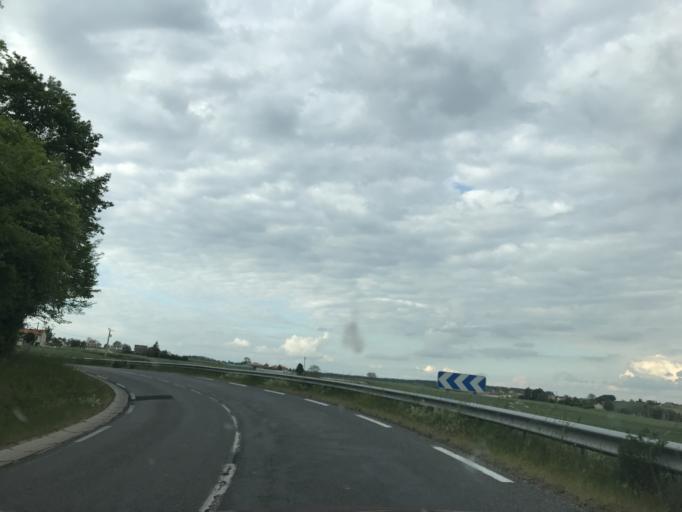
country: FR
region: Auvergne
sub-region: Departement du Puy-de-Dome
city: Randan
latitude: 45.9908
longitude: 3.3548
